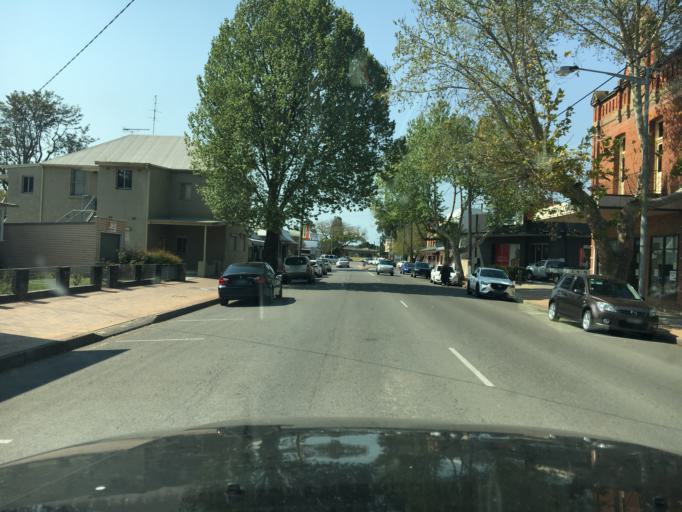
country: AU
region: New South Wales
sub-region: Singleton
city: Singleton
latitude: -32.5614
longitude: 151.1709
